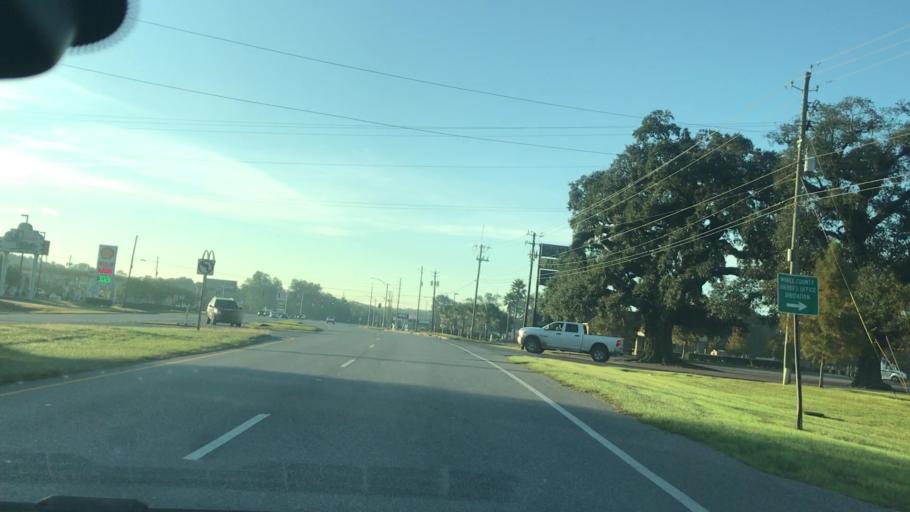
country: US
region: Alabama
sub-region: Mobile County
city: Theodore
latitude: 30.5567
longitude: -88.1728
